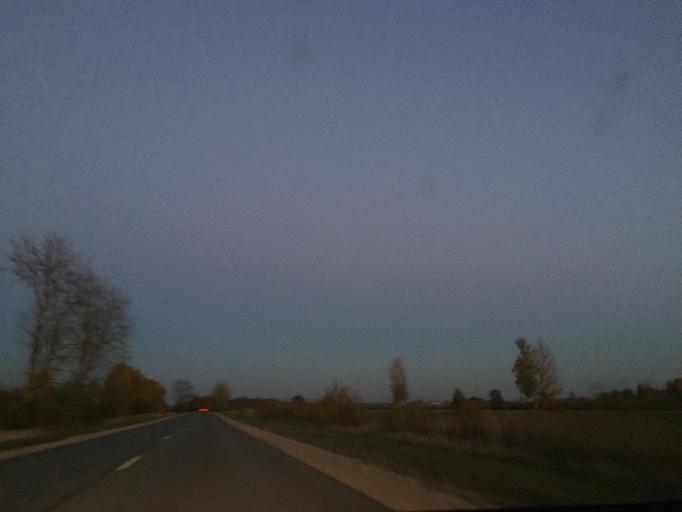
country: LT
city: Zagare
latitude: 56.4828
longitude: 23.1130
